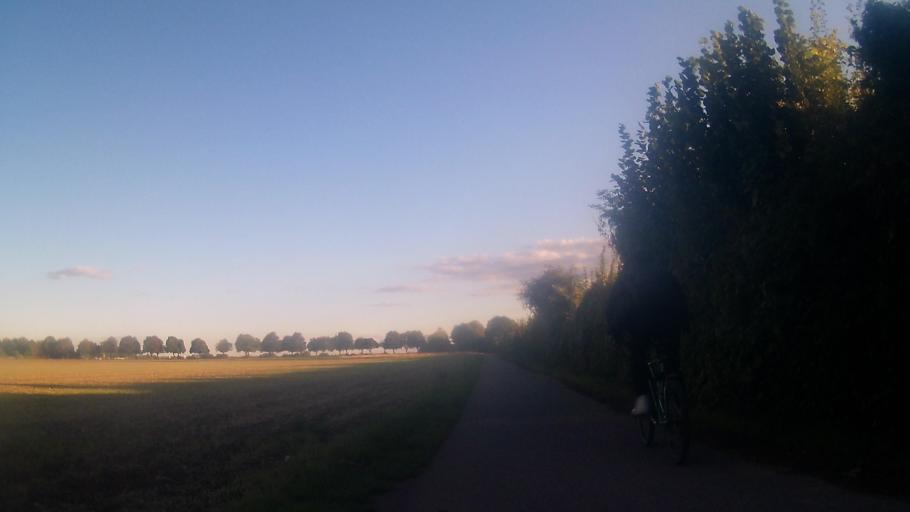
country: DE
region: Rheinland-Pfalz
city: Worms
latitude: 49.6265
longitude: 8.3397
